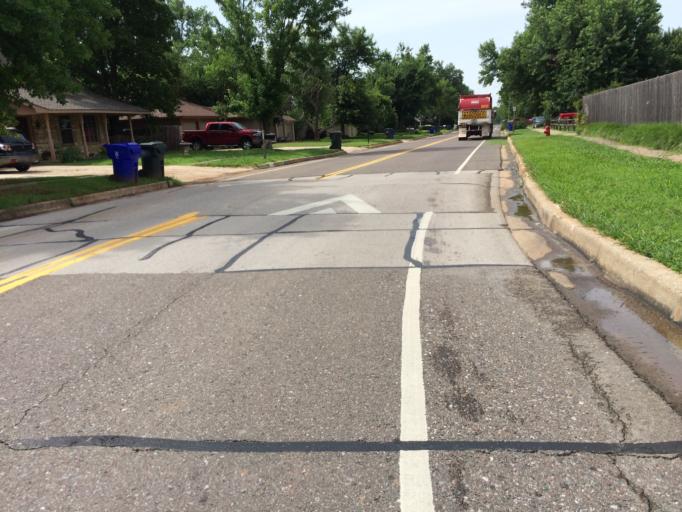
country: US
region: Oklahoma
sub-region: Cleveland County
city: Norman
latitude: 35.1999
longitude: -97.4110
